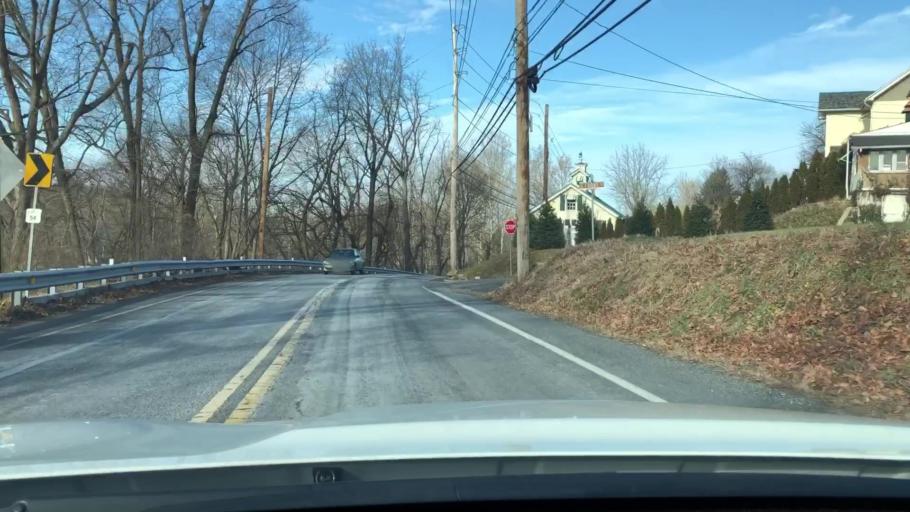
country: US
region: Pennsylvania
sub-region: Lehigh County
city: Catasauqua
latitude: 40.6451
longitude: -75.4645
